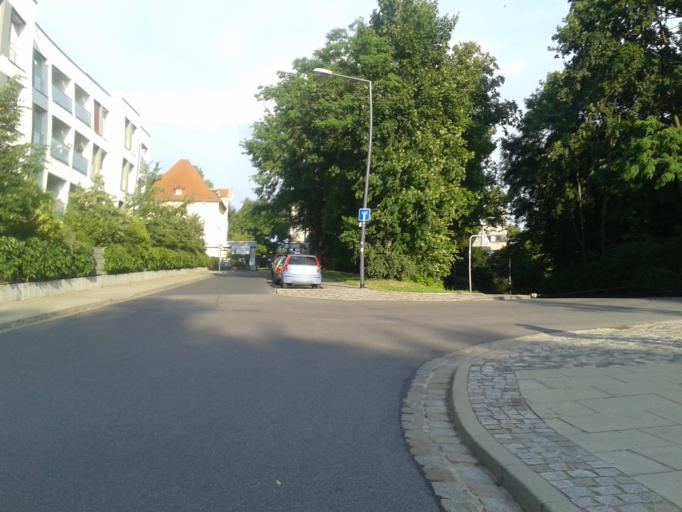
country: DE
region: Saxony
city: Albertstadt
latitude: 51.0726
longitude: 13.7573
